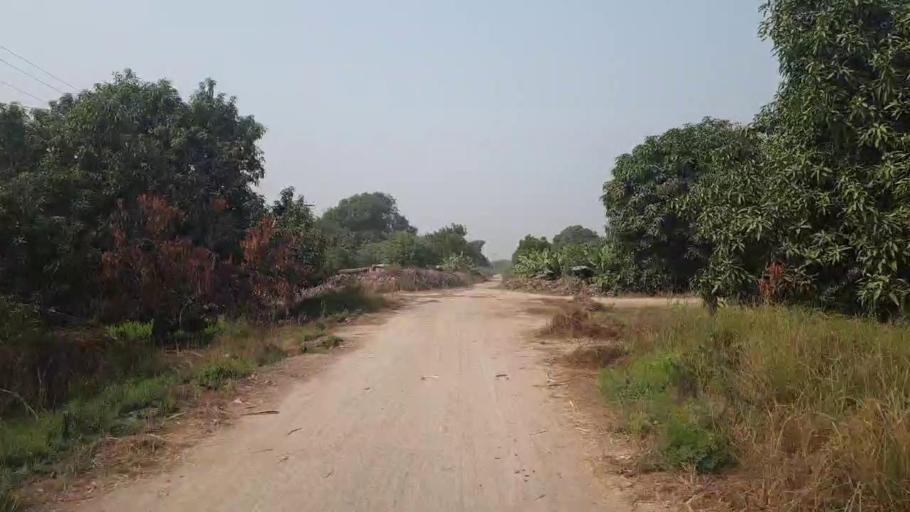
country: PK
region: Sindh
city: Tando Muhammad Khan
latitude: 25.2685
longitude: 68.5828
